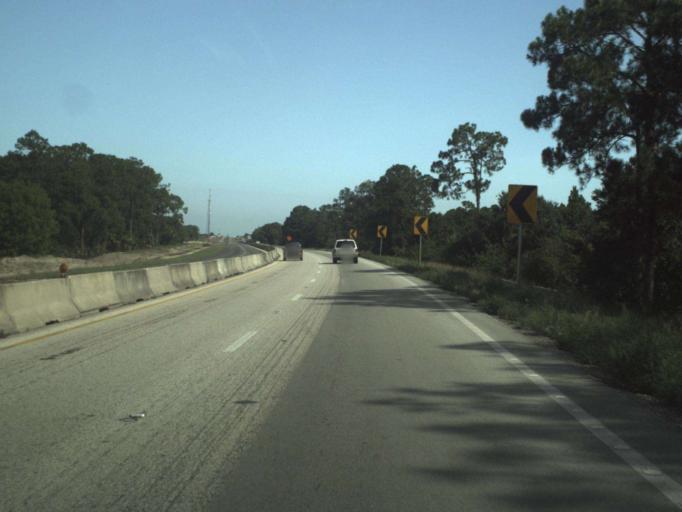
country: US
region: Florida
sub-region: Indian River County
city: Roseland
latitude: 27.8164
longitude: -80.5493
